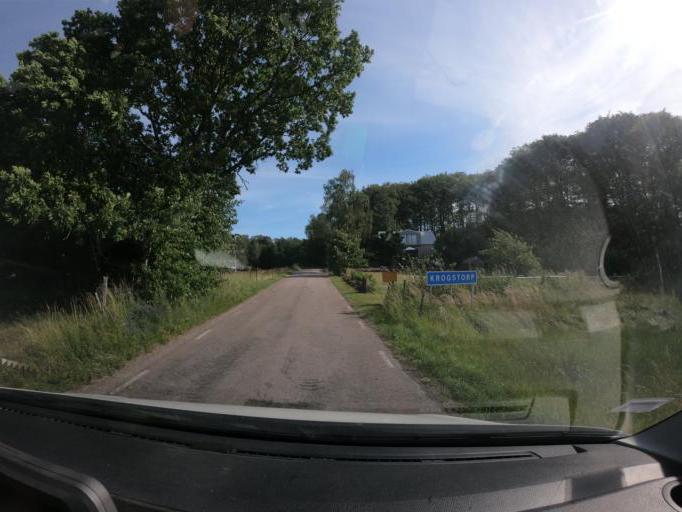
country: SE
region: Skane
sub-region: Bastads Kommun
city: Forslov
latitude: 56.3769
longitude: 12.7982
